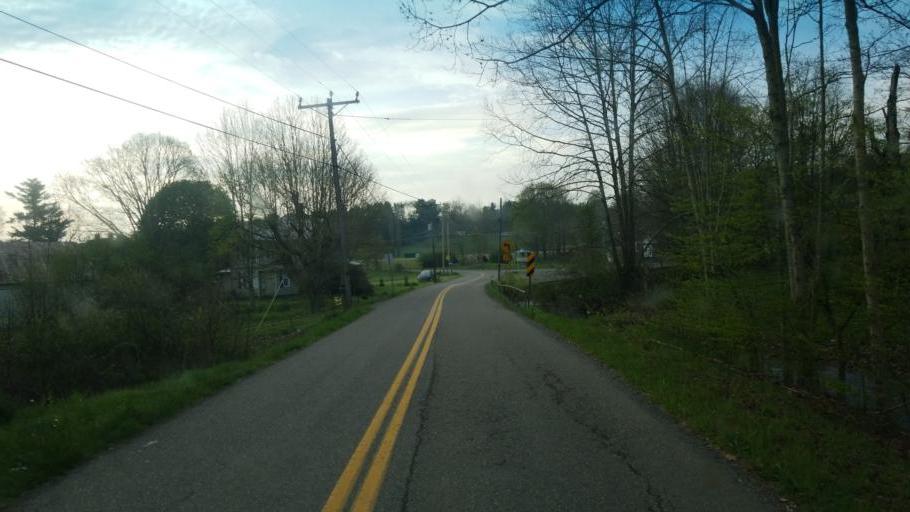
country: US
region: Virginia
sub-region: Smyth County
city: Atkins
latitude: 36.7740
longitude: -81.4201
